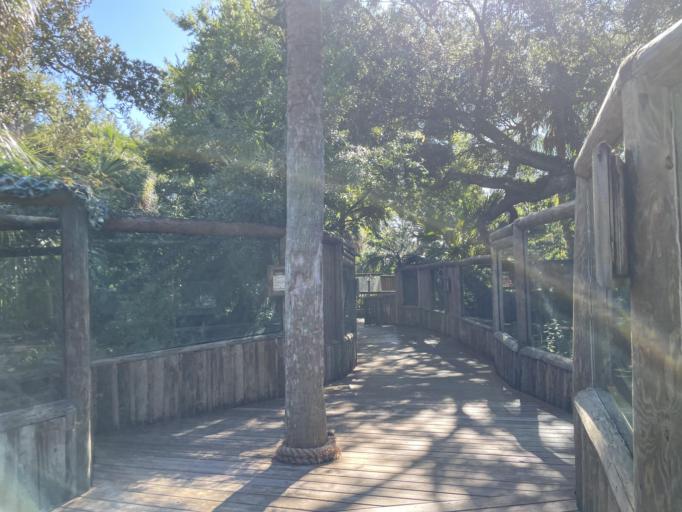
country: US
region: Florida
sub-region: Saint Johns County
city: Saint Augustine
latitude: 29.8814
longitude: -81.2891
